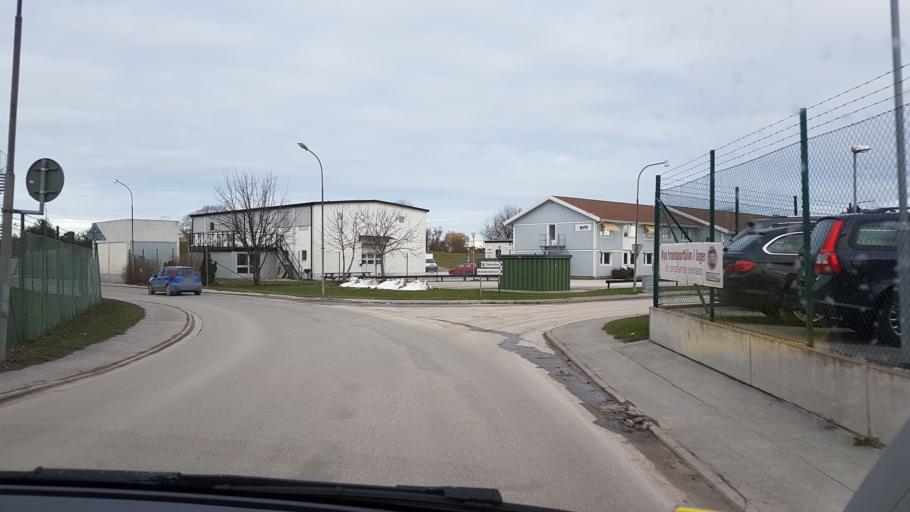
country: SE
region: Gotland
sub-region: Gotland
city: Visby
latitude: 57.6459
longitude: 18.3159
